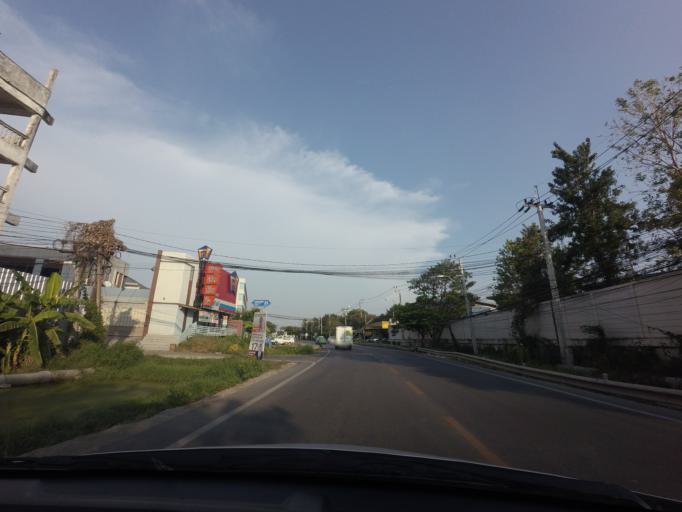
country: TH
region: Bangkok
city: Suan Luang
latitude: 13.7428
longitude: 100.6747
